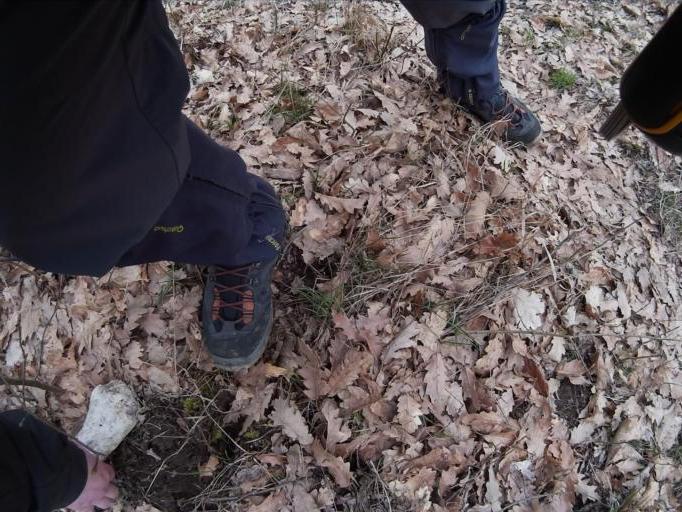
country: HU
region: Veszprem
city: Zirc
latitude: 47.1859
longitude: 17.9165
